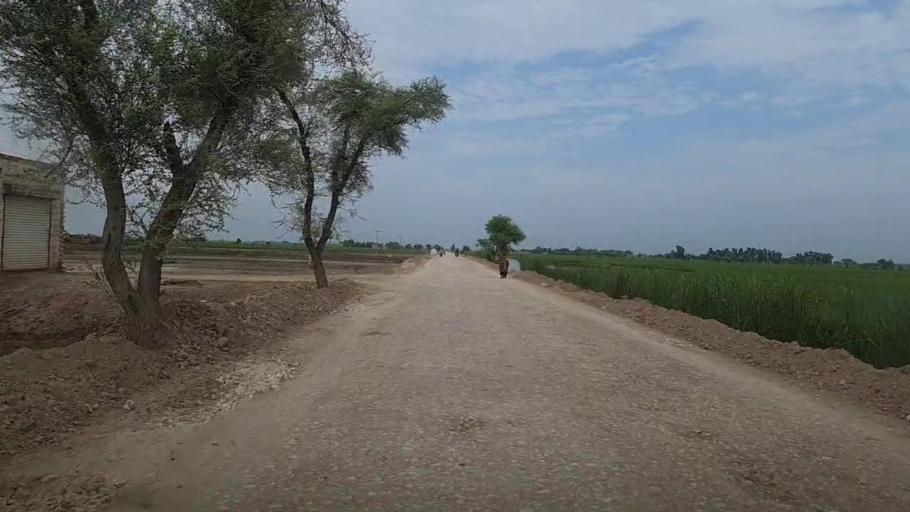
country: PK
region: Sindh
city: Thul
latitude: 28.2497
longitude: 68.7948
